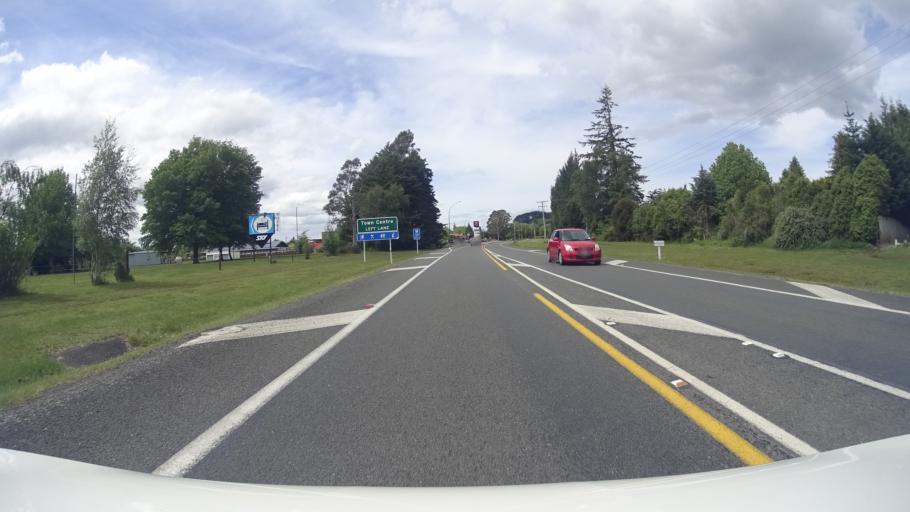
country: NZ
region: Waikato
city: Turangi
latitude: -38.9925
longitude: 175.8080
